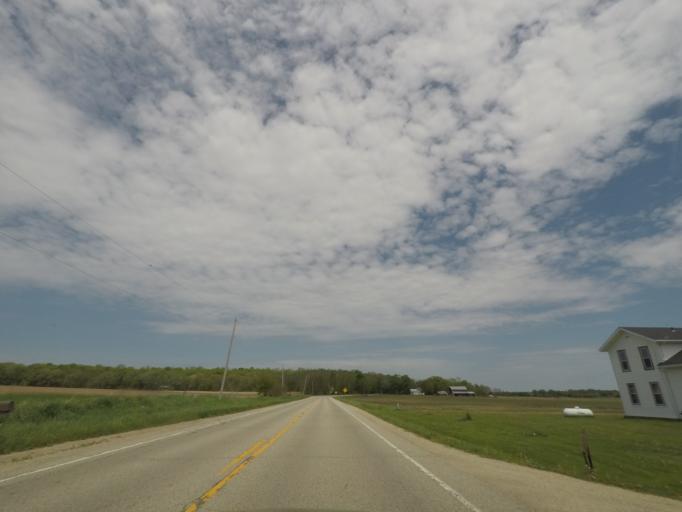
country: US
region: Wisconsin
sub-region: Rock County
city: Evansville
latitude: 42.7228
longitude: -89.2889
